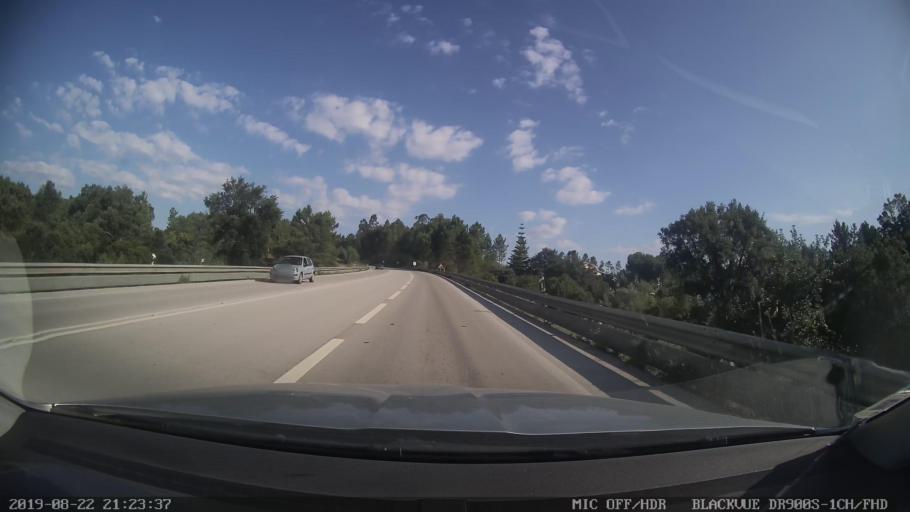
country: PT
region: Castelo Branco
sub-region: Serta
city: Serta
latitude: 39.8331
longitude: -8.1105
